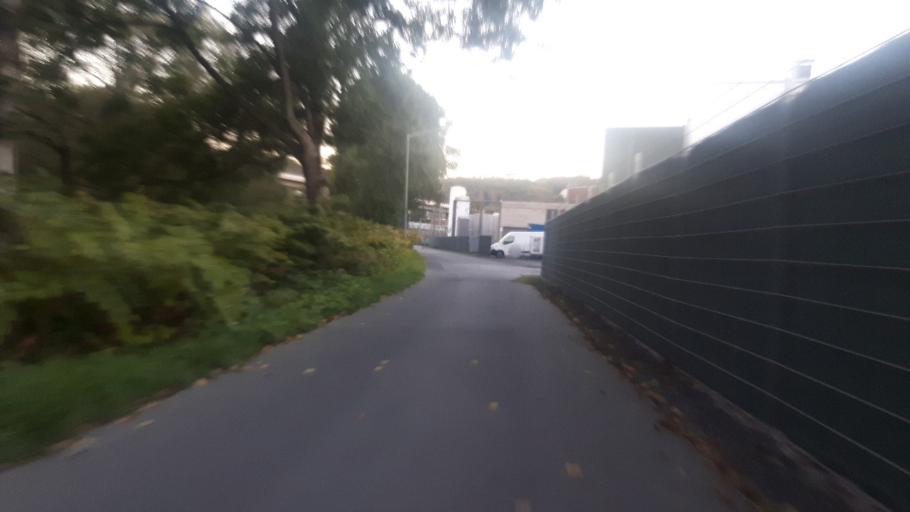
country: DE
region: North Rhine-Westphalia
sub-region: Regierungsbezirk Arnsberg
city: Siegen
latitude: 50.8632
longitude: 8.0085
